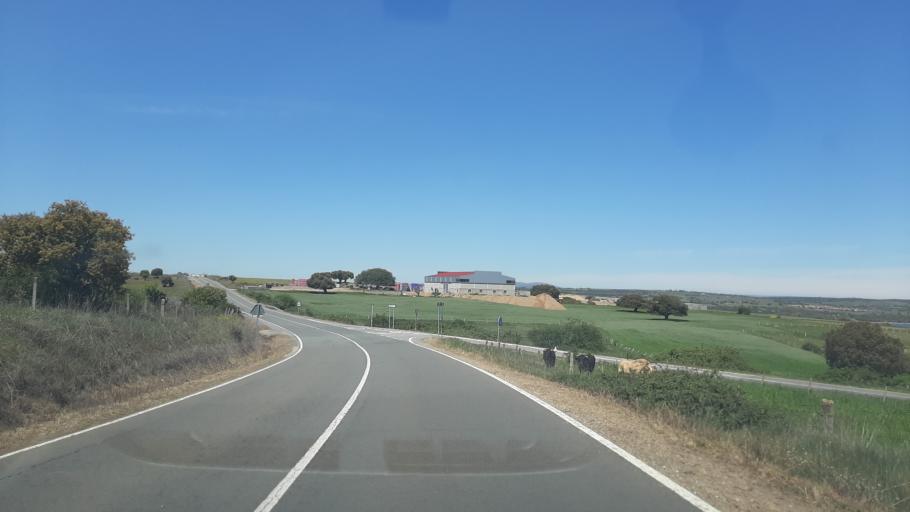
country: ES
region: Castille and Leon
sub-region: Provincia de Salamanca
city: Aldeavieja de Tormes
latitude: 40.5470
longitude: -5.5962
